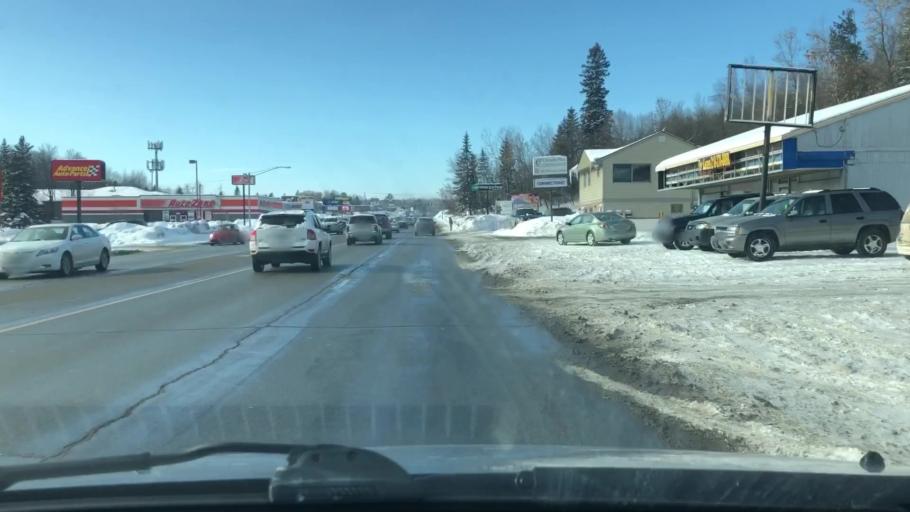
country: US
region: Minnesota
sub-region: Saint Louis County
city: Duluth
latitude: 46.8005
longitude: -92.1254
